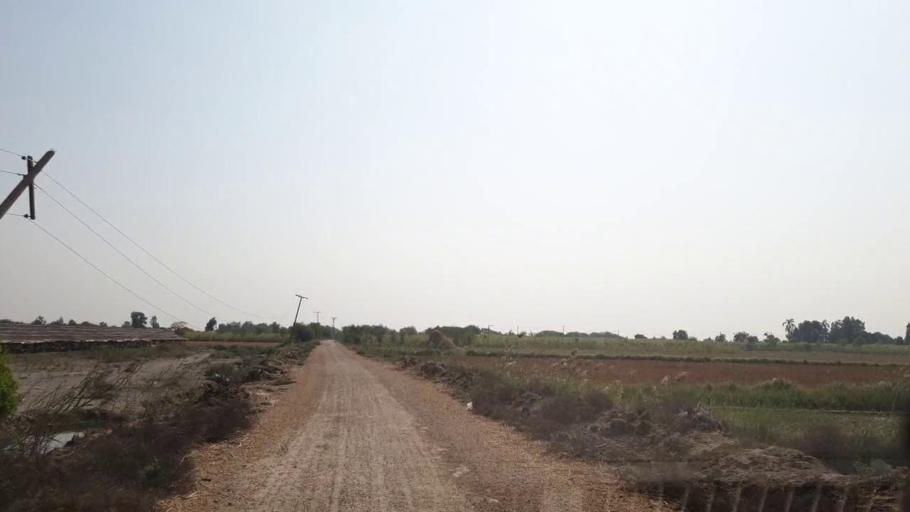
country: PK
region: Sindh
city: Tando Muhammad Khan
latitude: 25.0425
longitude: 68.4539
